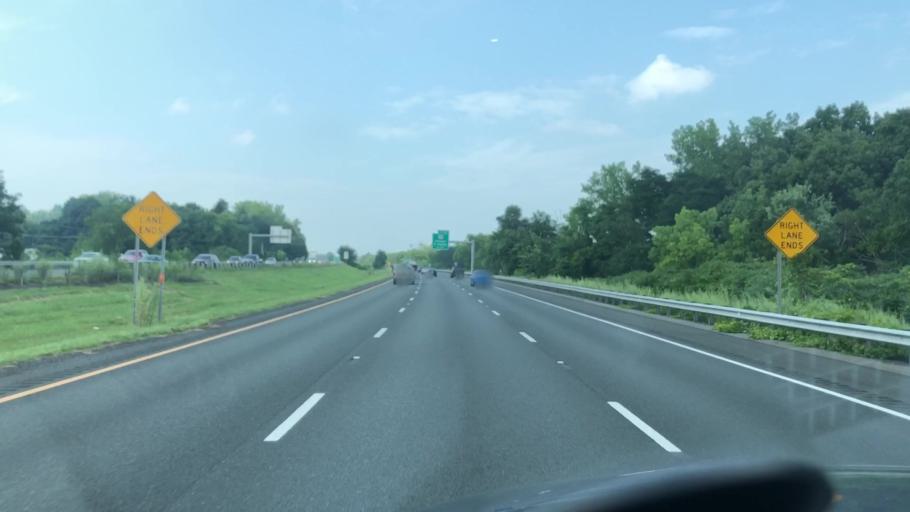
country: US
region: Massachusetts
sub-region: Hampden County
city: Holyoke
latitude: 42.1884
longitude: -72.6385
